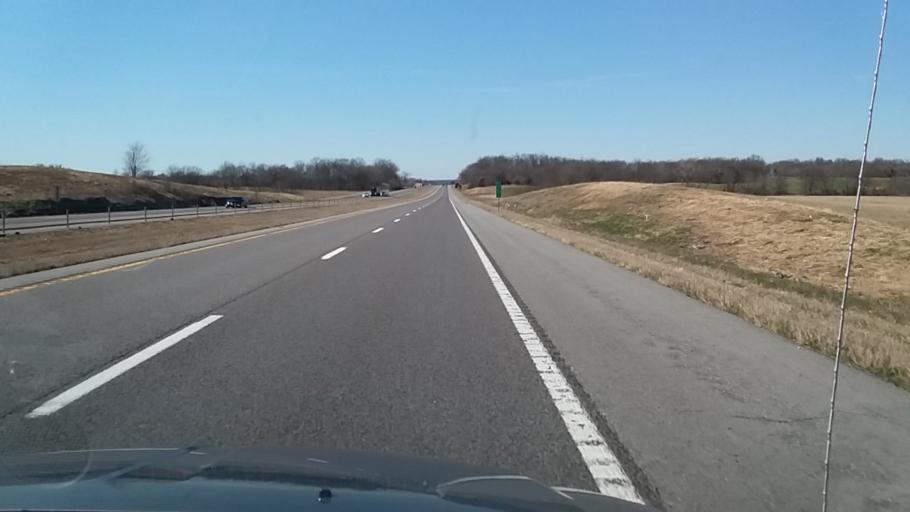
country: US
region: Missouri
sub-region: Cape Girardeau County
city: Jackson
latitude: 37.5560
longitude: -89.7394
